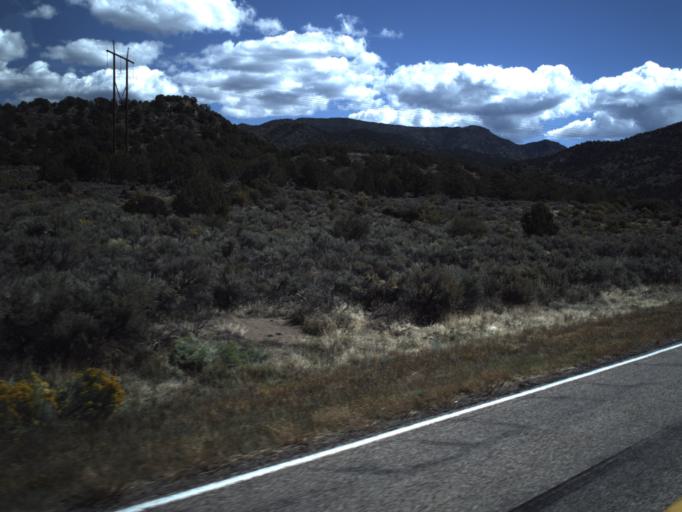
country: US
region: Utah
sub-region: Washington County
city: Enterprise
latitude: 37.4589
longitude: -113.6296
